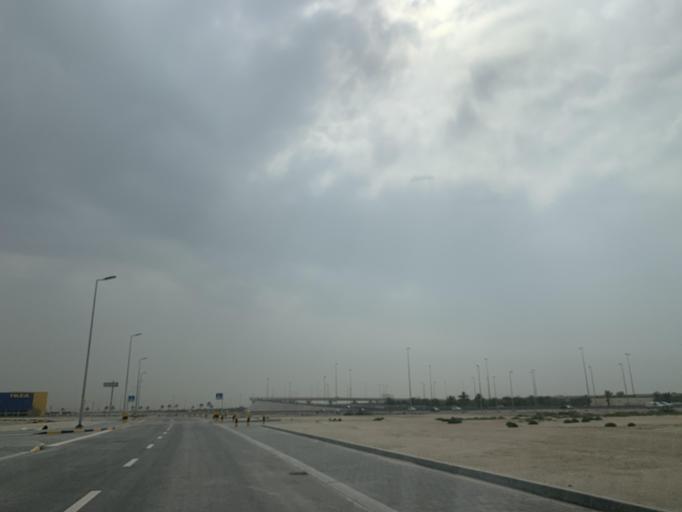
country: BH
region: Northern
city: Madinat `Isa
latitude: 26.1856
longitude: 50.5080
